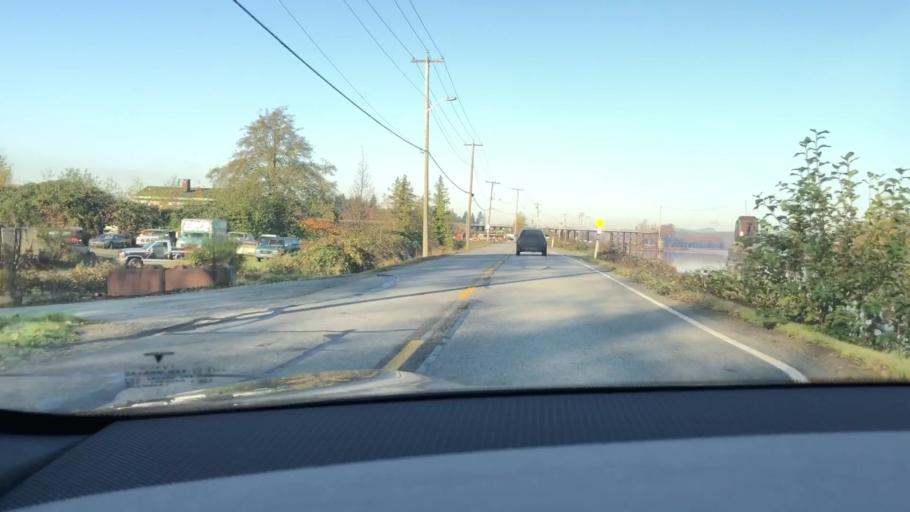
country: CA
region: British Columbia
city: New Westminster
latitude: 49.1801
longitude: -122.9832
